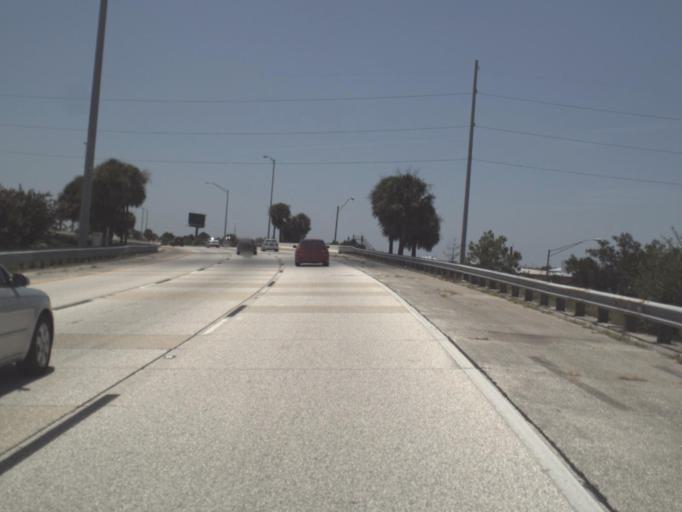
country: US
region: Florida
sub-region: Pinellas County
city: Saint Petersburg
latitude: 27.7614
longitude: -82.6700
